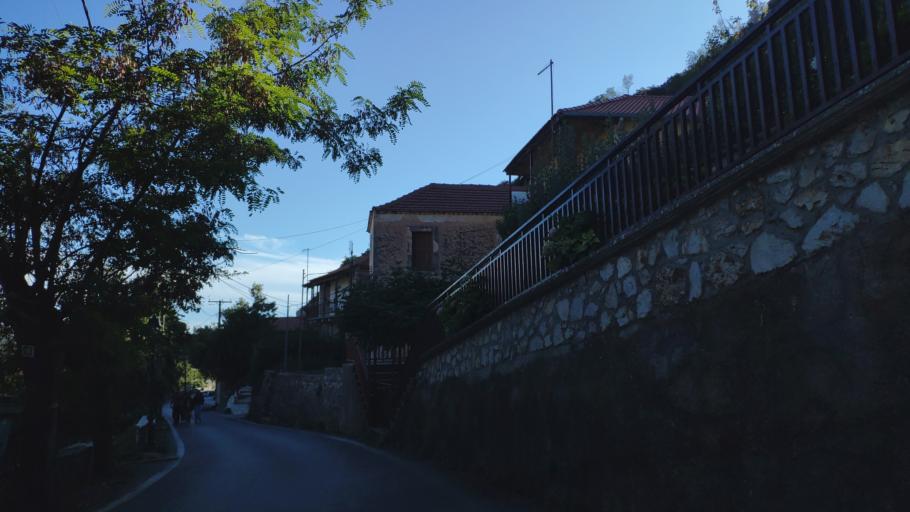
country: GR
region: Peloponnese
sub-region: Nomos Arkadias
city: Dimitsana
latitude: 37.5539
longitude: 22.0781
